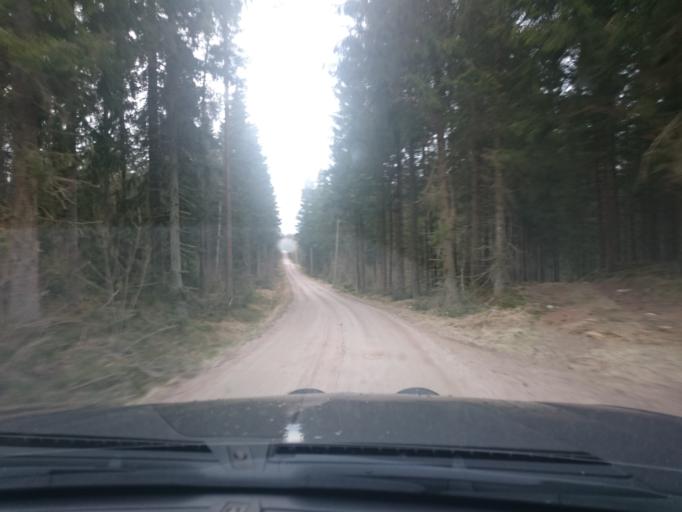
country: SE
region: Joenkoeping
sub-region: Vetlanda Kommun
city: Vetlanda
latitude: 57.2933
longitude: 15.1470
